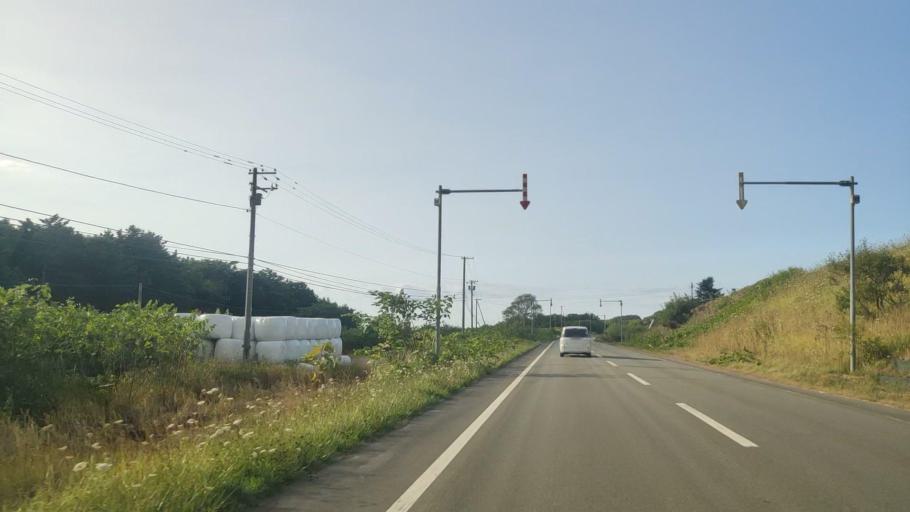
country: JP
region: Hokkaido
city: Makubetsu
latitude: 45.0562
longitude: 141.7490
